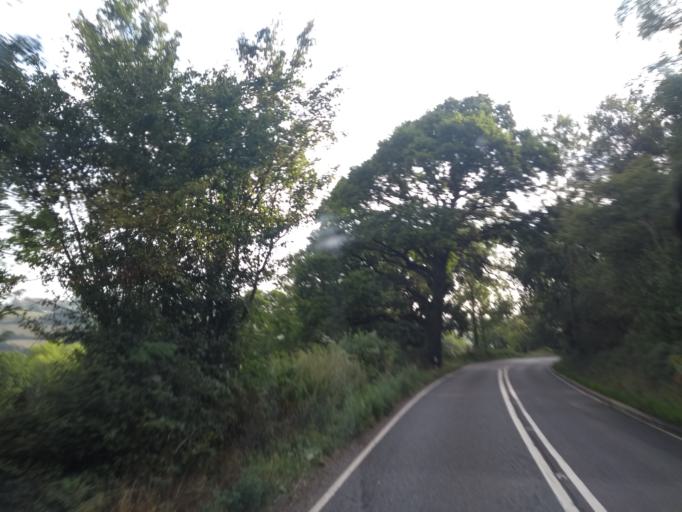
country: GB
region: England
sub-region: Devon
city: Colyton
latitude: 50.7865
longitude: -3.0612
